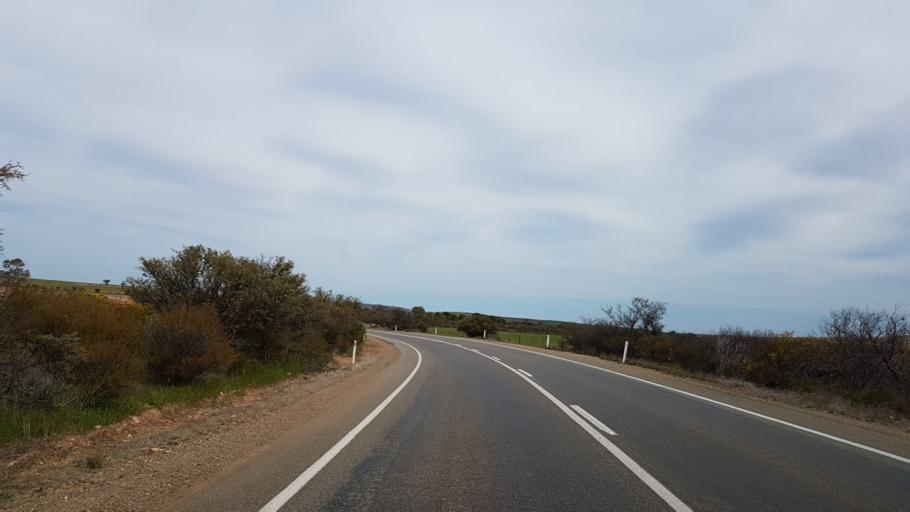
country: AU
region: South Australia
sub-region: Northern Areas
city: Jamestown
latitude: -33.2322
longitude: 138.3921
